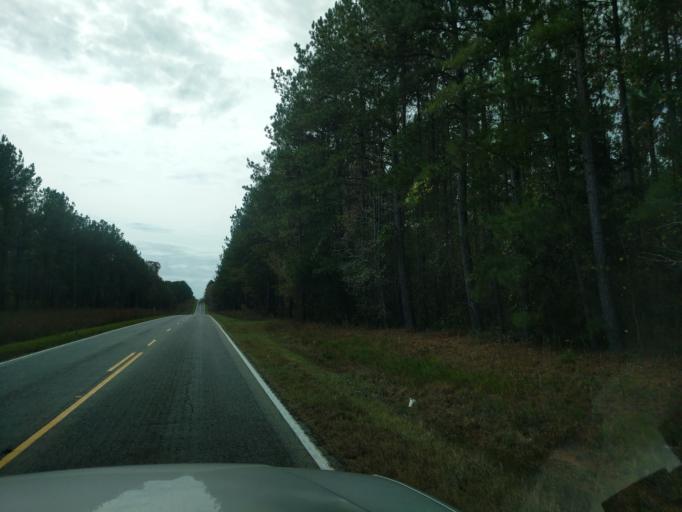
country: US
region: South Carolina
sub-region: Laurens County
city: Joanna
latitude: 34.3081
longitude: -81.8433
